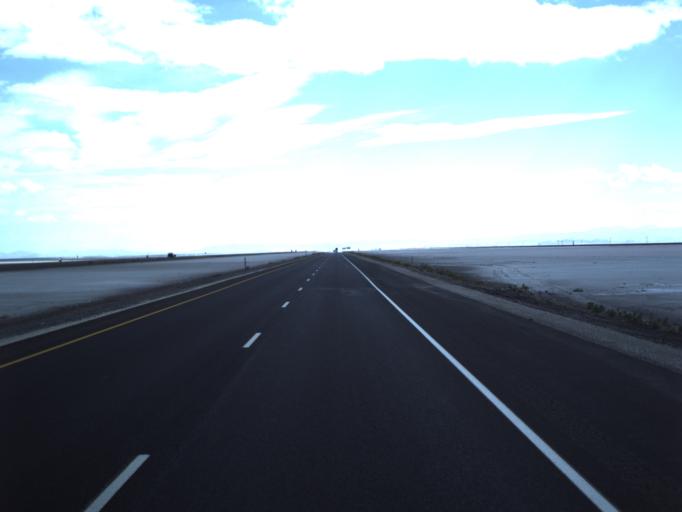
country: US
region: Utah
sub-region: Tooele County
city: Wendover
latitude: 40.7322
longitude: -113.5550
